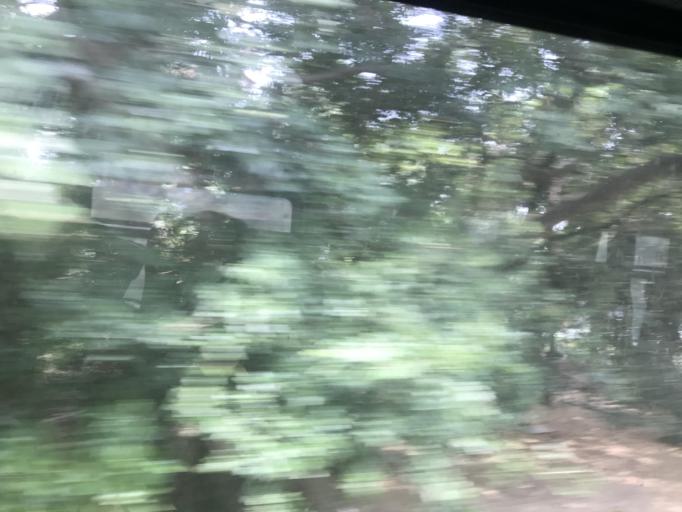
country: LK
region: Northern Province
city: Kilinochchi
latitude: 9.5769
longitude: 80.3564
